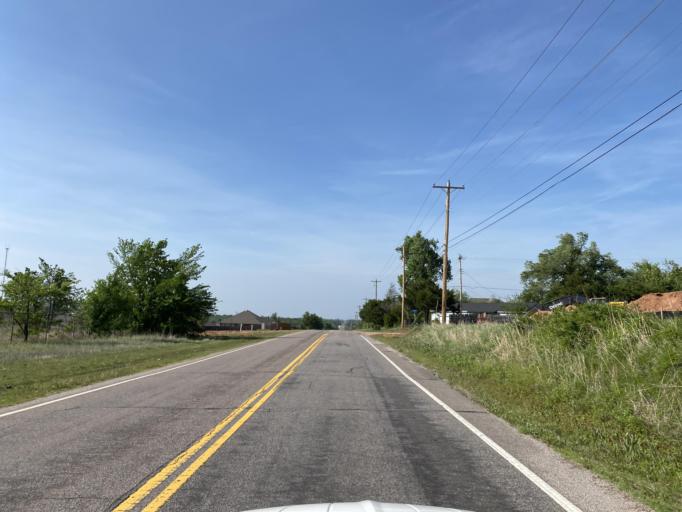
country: US
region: Oklahoma
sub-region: Oklahoma County
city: Nicoma Park
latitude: 35.4366
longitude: -97.3357
